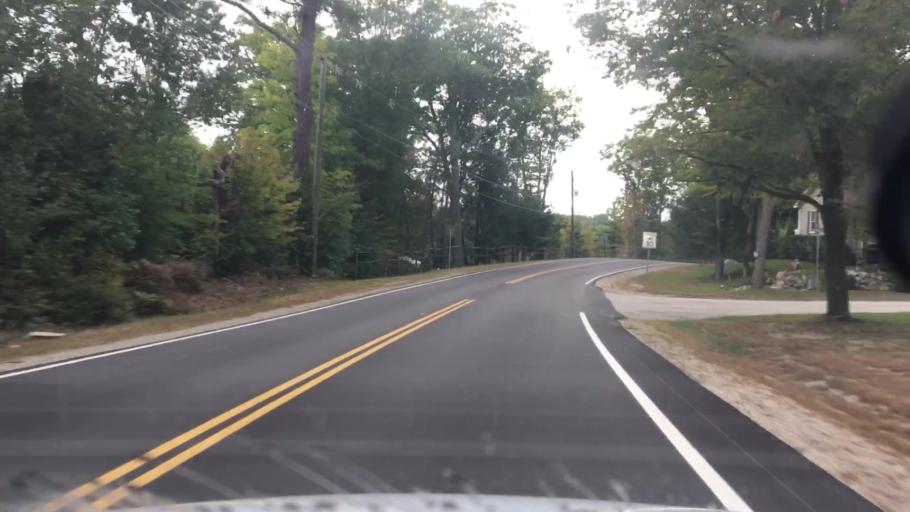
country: US
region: New Hampshire
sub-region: Carroll County
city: Sanbornville
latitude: 43.5482
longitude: -71.0274
